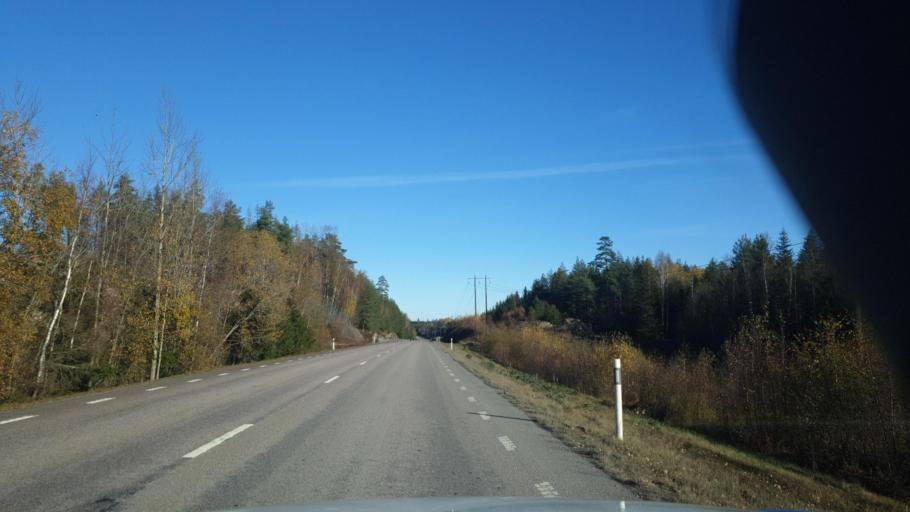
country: SE
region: Vaermland
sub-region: Karlstads Kommun
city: Edsvalla
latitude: 59.4189
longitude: 13.1885
